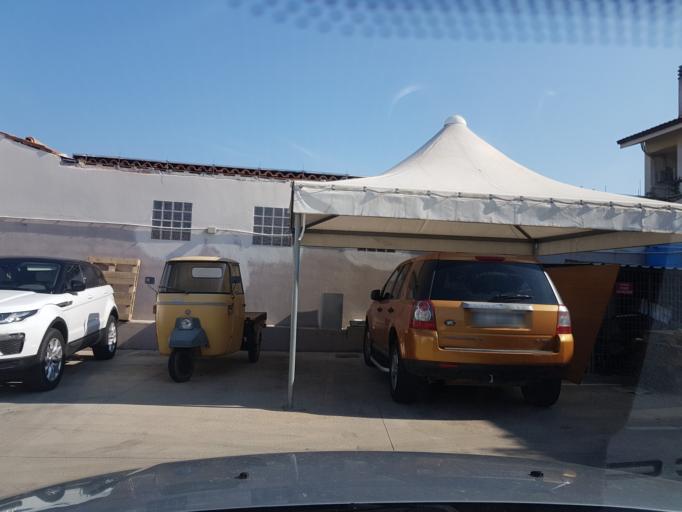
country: IT
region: Sardinia
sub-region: Provincia di Oristano
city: Oristano
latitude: 39.9009
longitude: 8.5992
